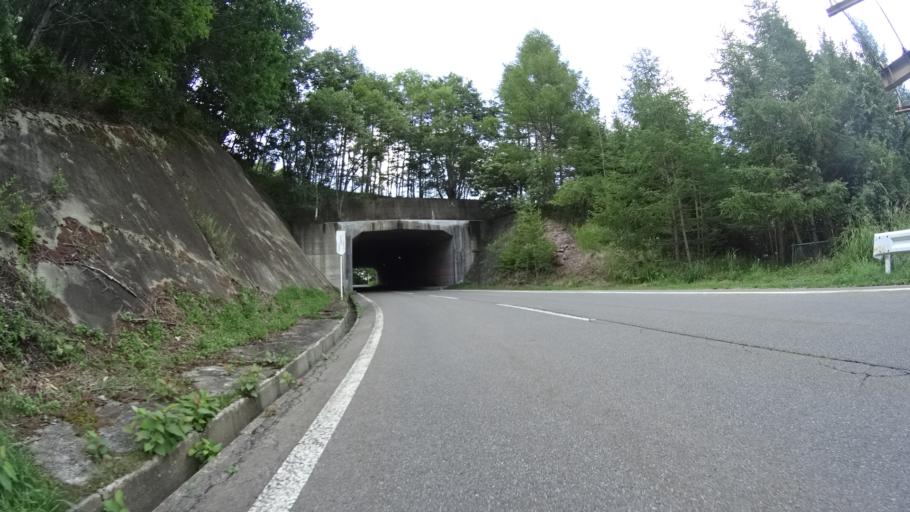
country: JP
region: Nagano
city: Saku
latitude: 36.0528
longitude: 138.4038
